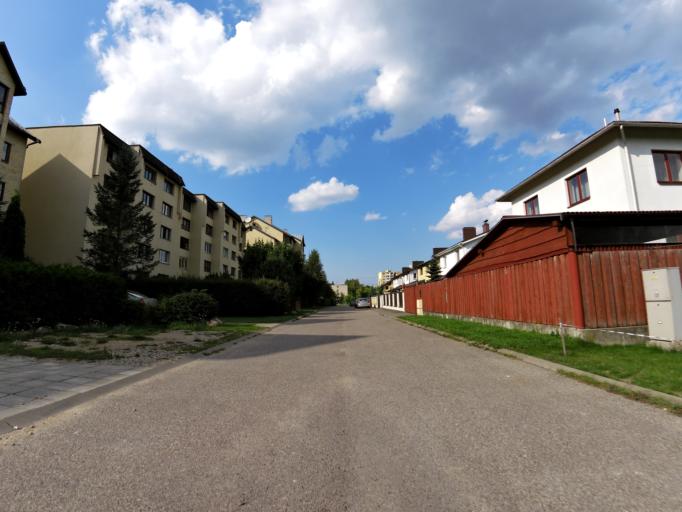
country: LT
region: Vilnius County
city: Lazdynai
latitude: 54.6652
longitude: 25.2175
